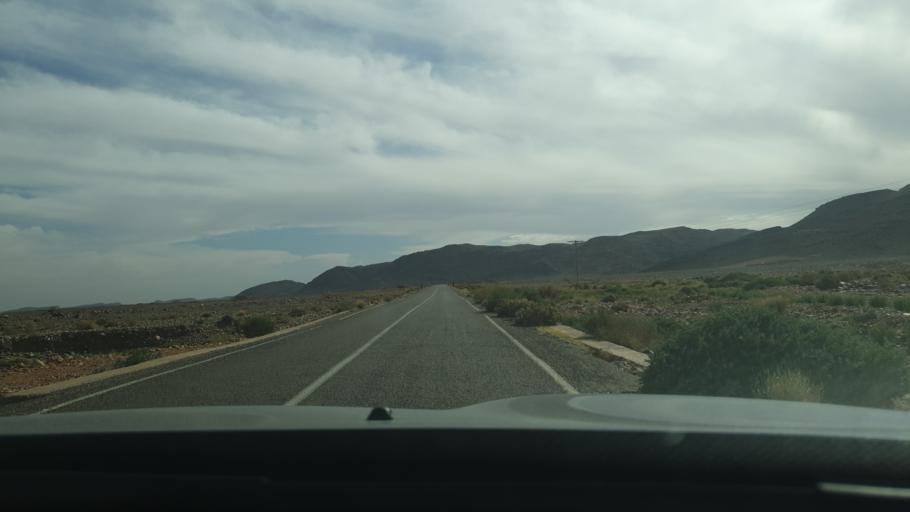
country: MA
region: Meknes-Tafilalet
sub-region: Errachidia
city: Fezna
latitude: 31.5335
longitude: -4.6423
